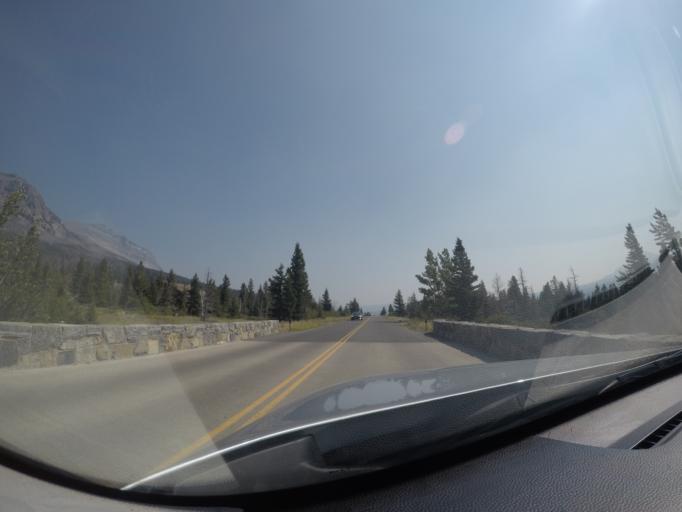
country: US
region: Montana
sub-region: Glacier County
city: Browning
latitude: 48.6936
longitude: -113.5188
